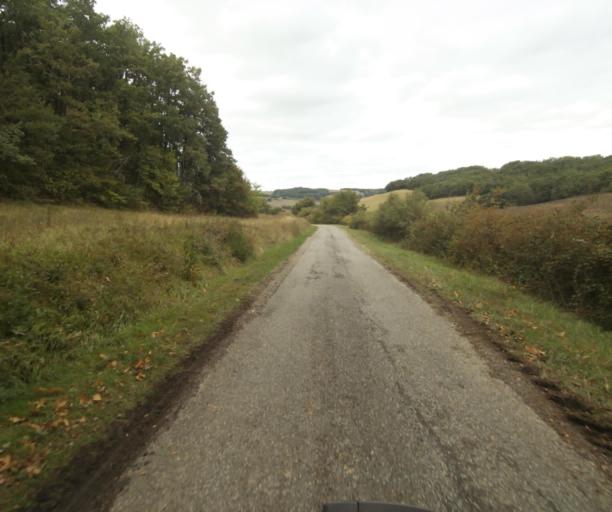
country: FR
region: Midi-Pyrenees
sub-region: Departement du Tarn-et-Garonne
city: Beaumont-de-Lomagne
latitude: 43.8439
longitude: 1.0918
